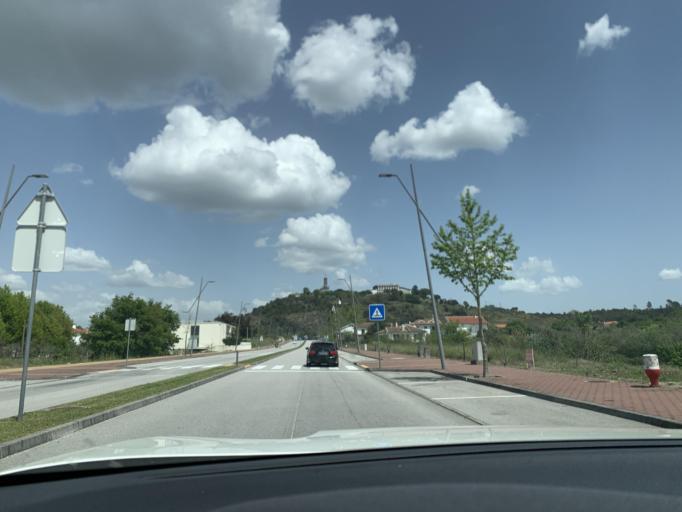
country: PT
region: Viseu
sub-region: Mangualde
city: Mangualde
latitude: 40.6094
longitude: -7.7531
